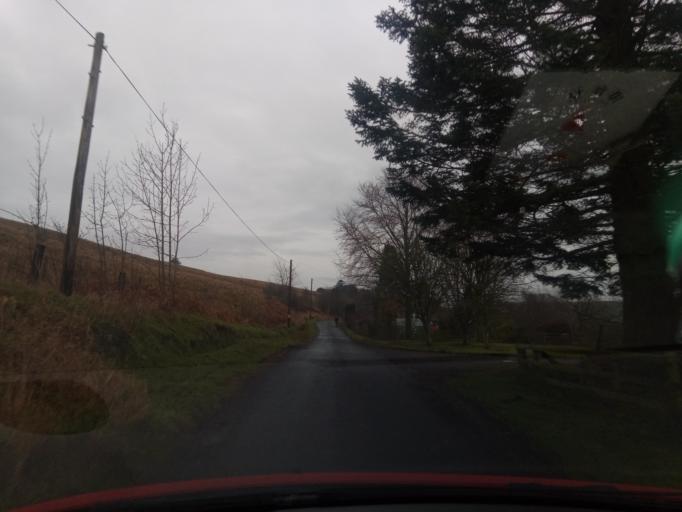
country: GB
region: England
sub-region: Northumberland
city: Rochester
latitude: 55.1803
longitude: -2.4327
